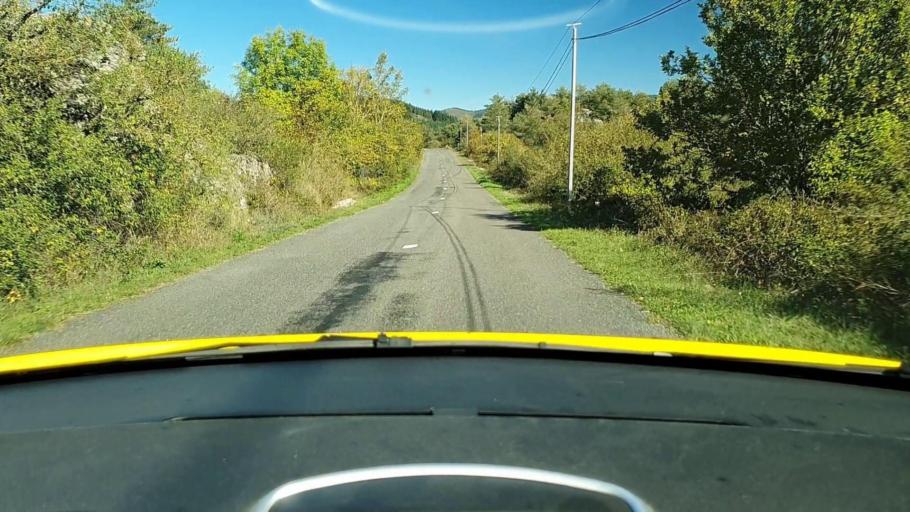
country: FR
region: Languedoc-Roussillon
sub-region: Departement du Gard
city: Le Vigan
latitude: 43.9641
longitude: 3.3945
